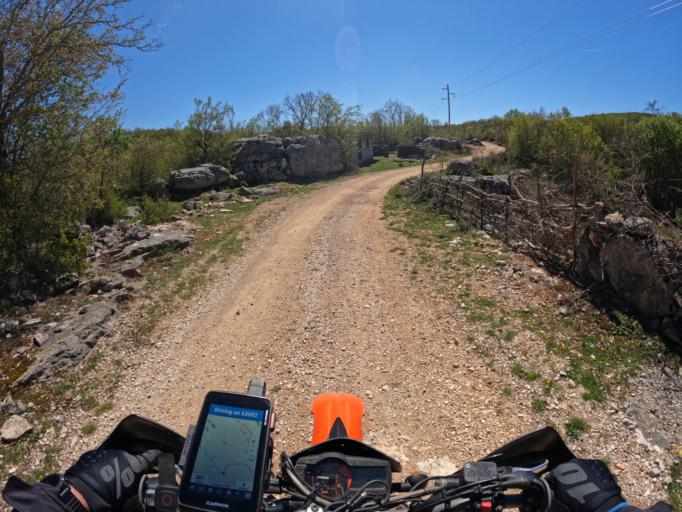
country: HR
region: Zadarska
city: Obrovac
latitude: 44.1436
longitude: 15.7525
